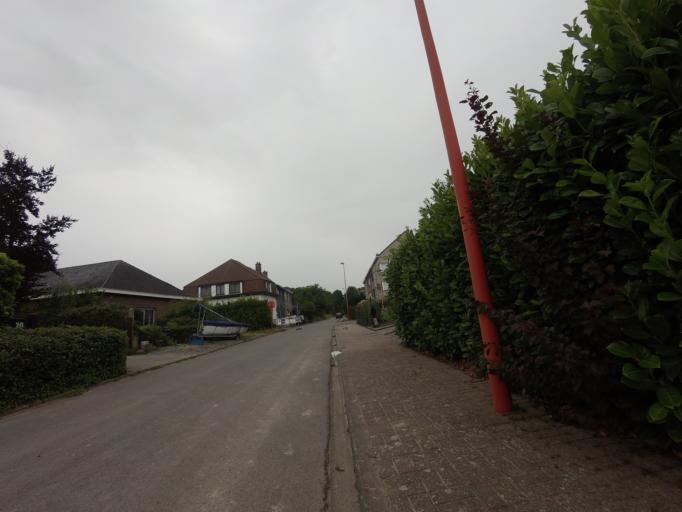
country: BE
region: Flanders
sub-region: Provincie Vlaams-Brabant
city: Grimbergen
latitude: 50.9393
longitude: 4.3770
